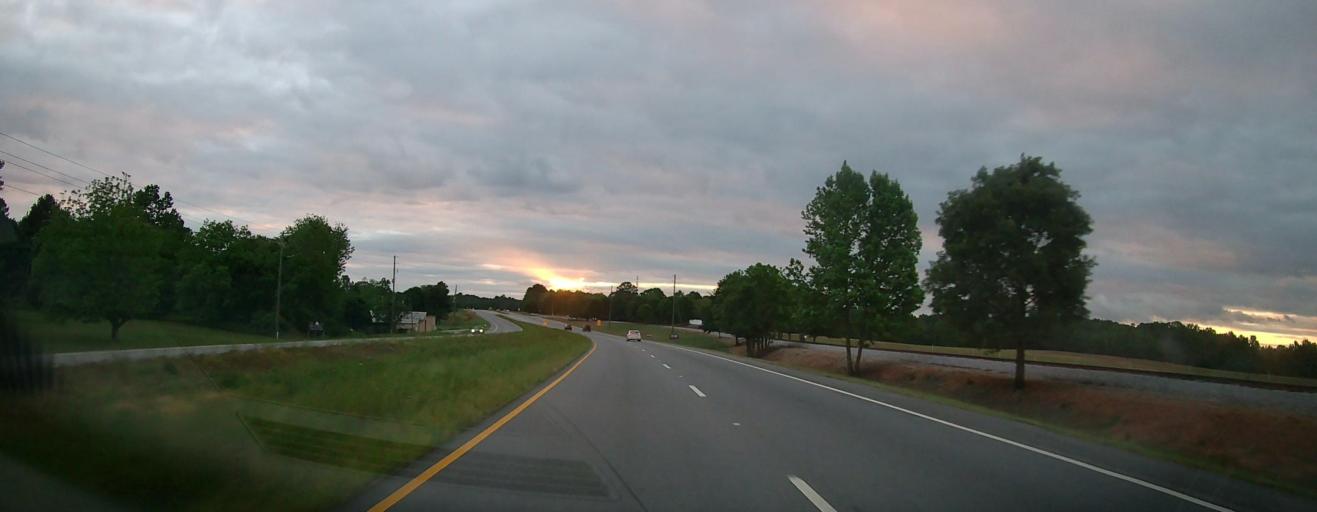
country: US
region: Georgia
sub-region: Clarke County
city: Country Club Estates
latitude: 34.0080
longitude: -83.4656
